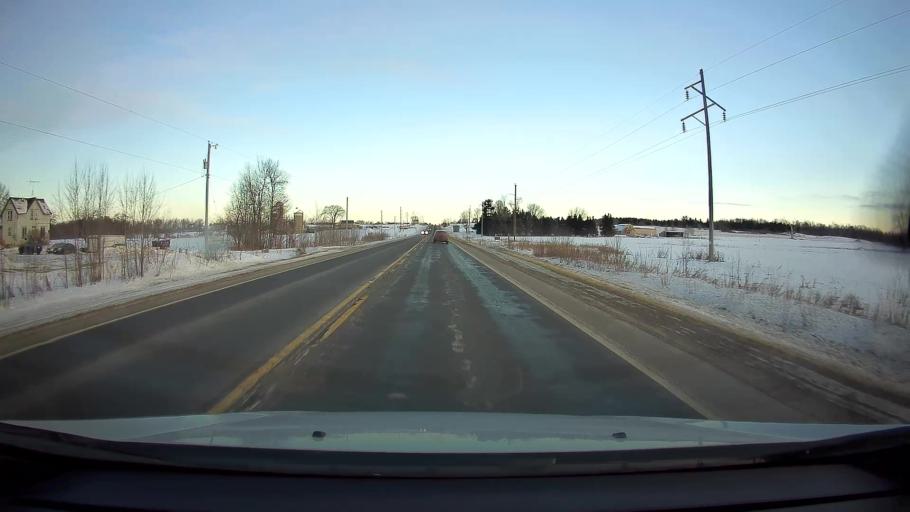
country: US
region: Wisconsin
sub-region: Barron County
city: Turtle Lake
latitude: 45.3638
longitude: -92.1669
